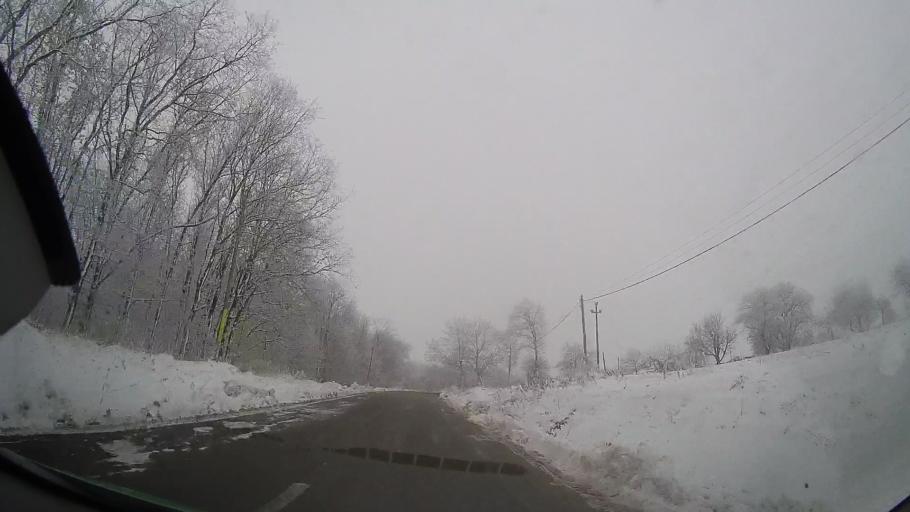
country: RO
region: Neamt
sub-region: Comuna Poenari
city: Poienari
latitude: 46.8908
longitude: 27.1373
